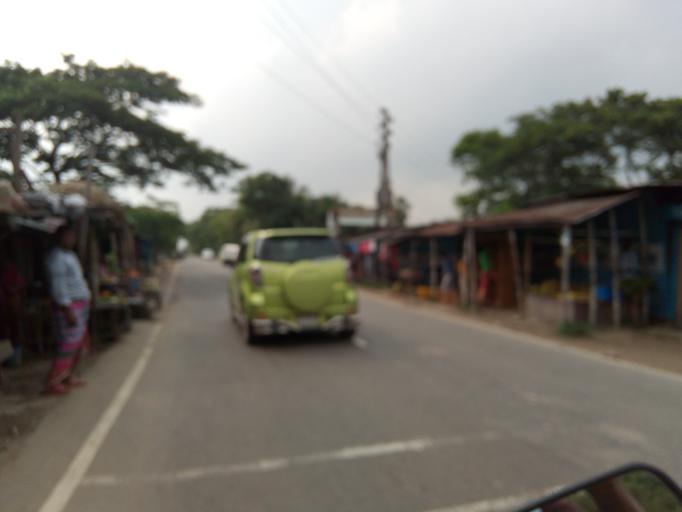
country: BD
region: Dhaka
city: Paltan
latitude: 23.7399
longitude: 90.4800
